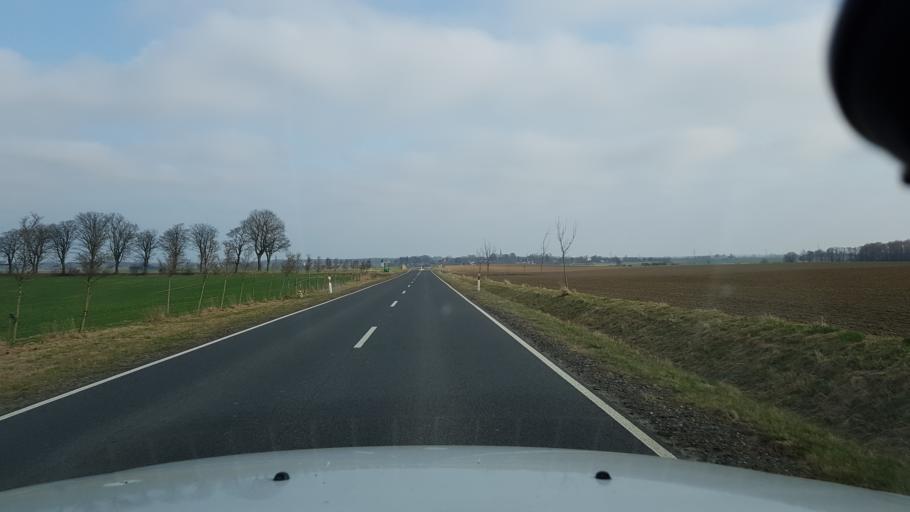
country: PL
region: West Pomeranian Voivodeship
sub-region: Powiat koszalinski
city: Sianow
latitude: 54.2792
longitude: 16.2702
